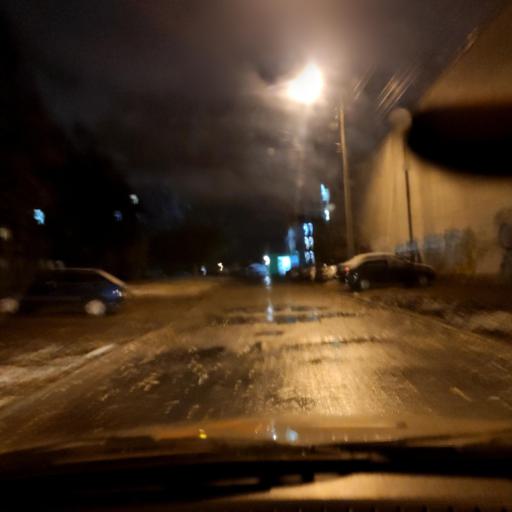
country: RU
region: Bashkortostan
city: Ufa
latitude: 54.7462
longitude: 55.9821
